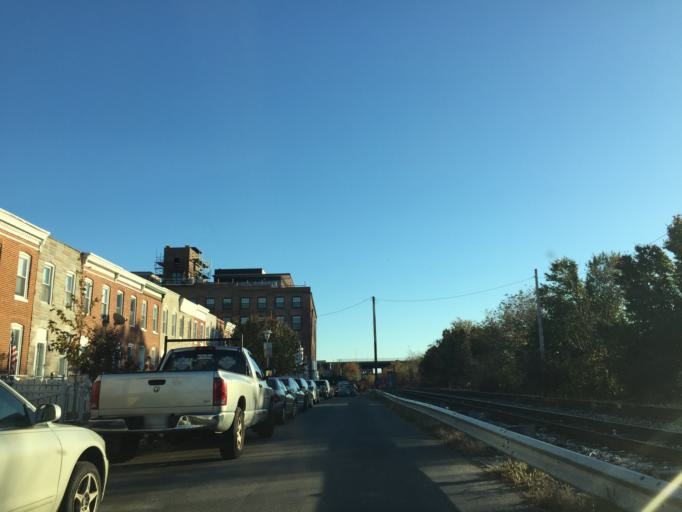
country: US
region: Maryland
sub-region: City of Baltimore
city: Baltimore
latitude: 39.2712
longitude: -76.6167
